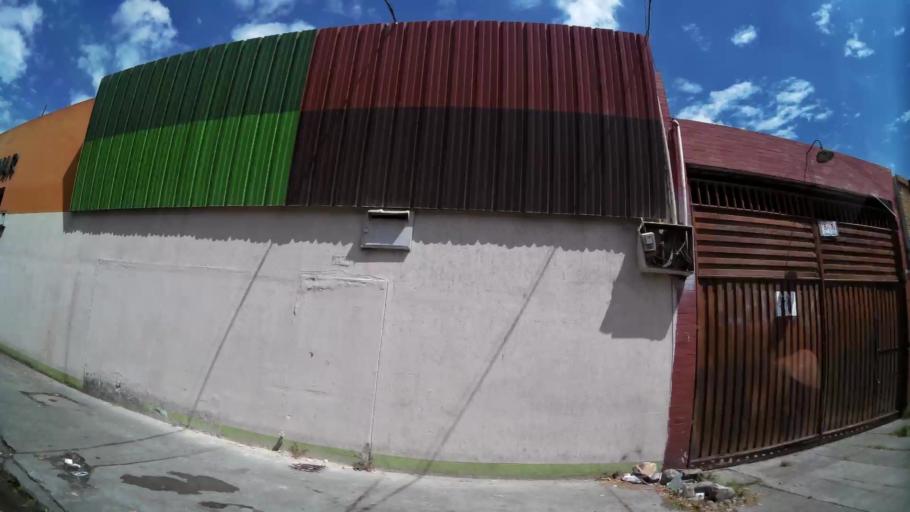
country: CO
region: Valle del Cauca
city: Cali
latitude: 3.4448
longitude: -76.5271
